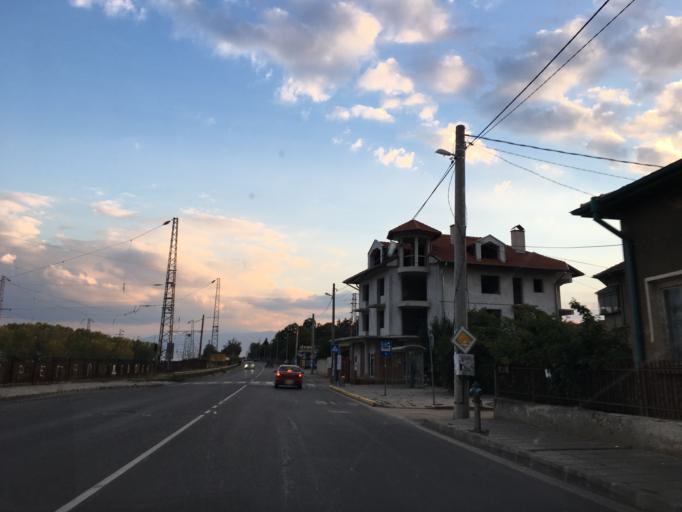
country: BG
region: Sofia-Capital
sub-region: Stolichna Obshtina
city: Sofia
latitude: 42.8157
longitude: 23.3523
